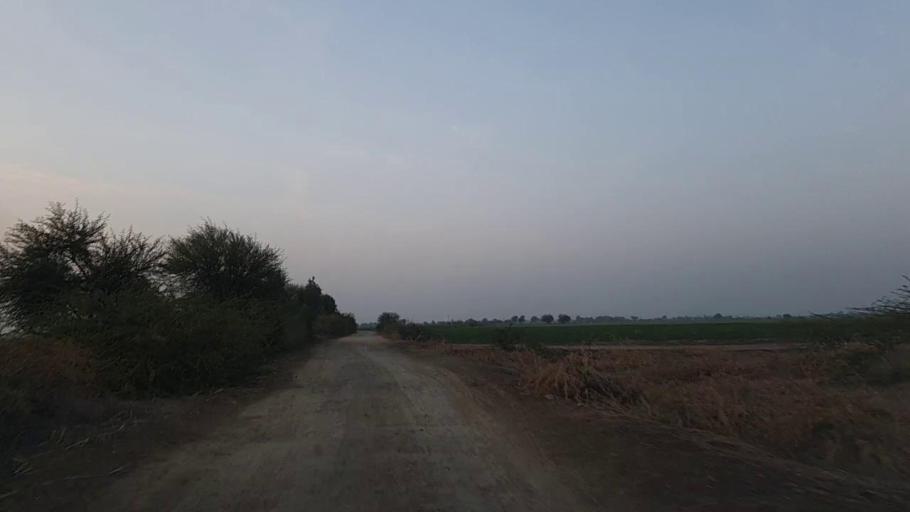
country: PK
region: Sindh
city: Naukot
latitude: 24.9831
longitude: 69.4264
